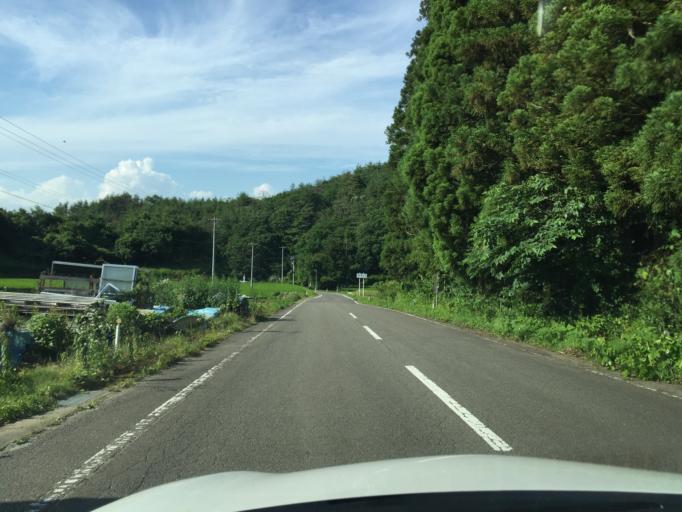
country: JP
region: Fukushima
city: Sukagawa
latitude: 37.2834
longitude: 140.5046
